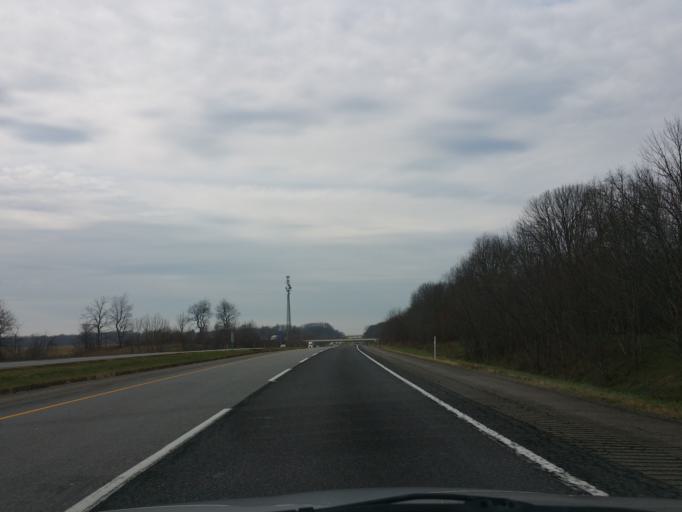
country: US
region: Indiana
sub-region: LaPorte County
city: LaPorte
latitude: 41.6223
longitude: -86.8070
